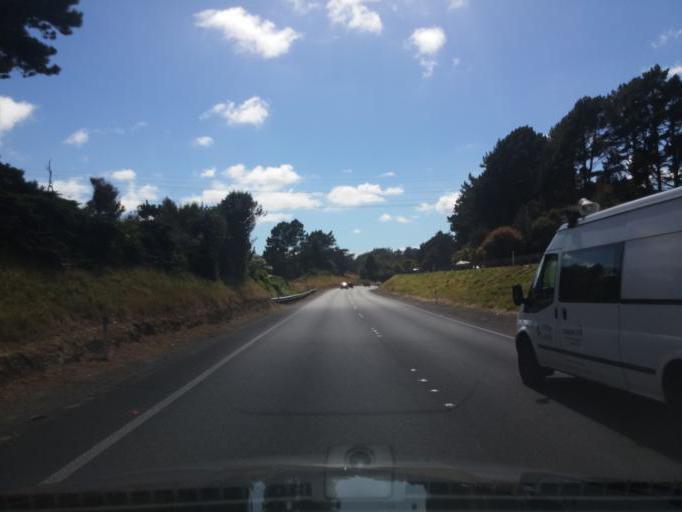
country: NZ
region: Wellington
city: Petone
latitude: -41.1971
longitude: 174.8249
